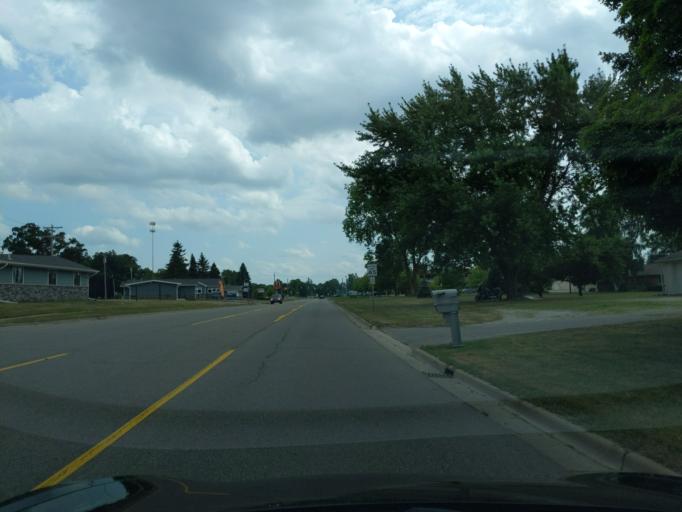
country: US
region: Michigan
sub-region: Eaton County
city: Eaton Rapids
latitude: 42.4969
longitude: -84.6573
